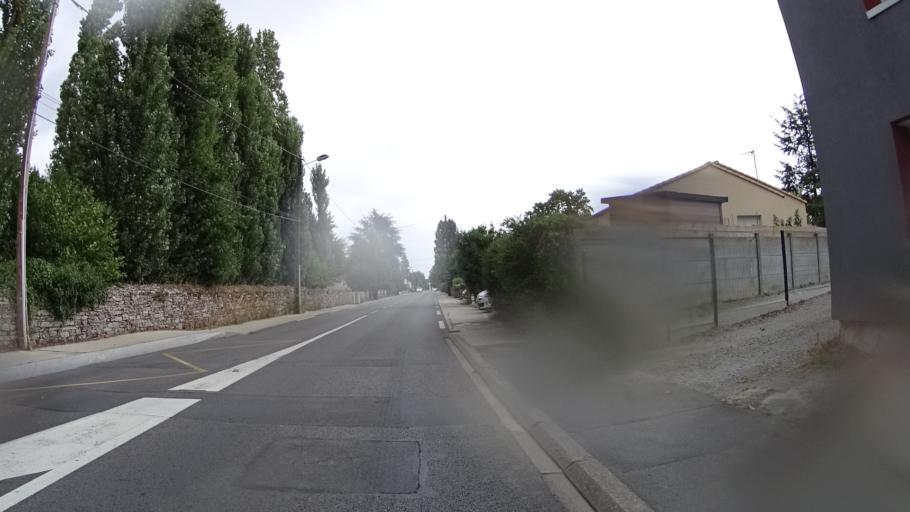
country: FR
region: Pays de la Loire
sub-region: Departement de la Loire-Atlantique
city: Indre
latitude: 47.1786
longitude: -1.6521
